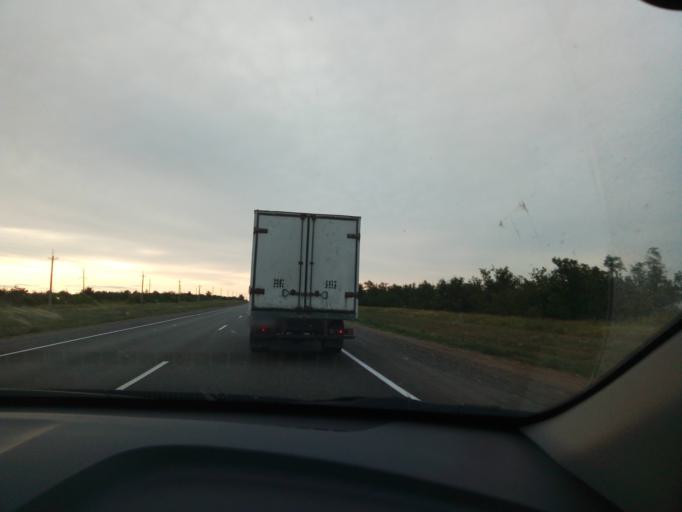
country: RU
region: Volgograd
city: Primorsk
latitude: 49.2291
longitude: 44.9020
